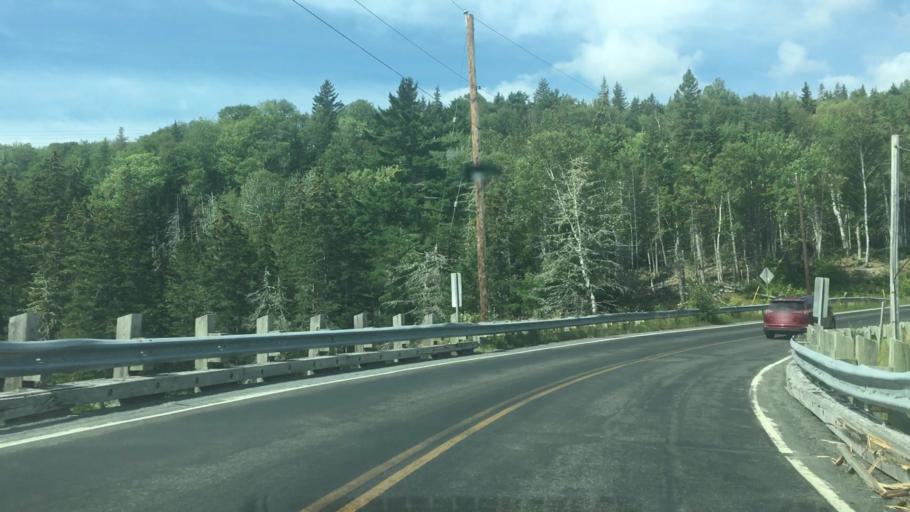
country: CA
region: Nova Scotia
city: Sydney Mines
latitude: 46.2061
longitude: -60.6220
